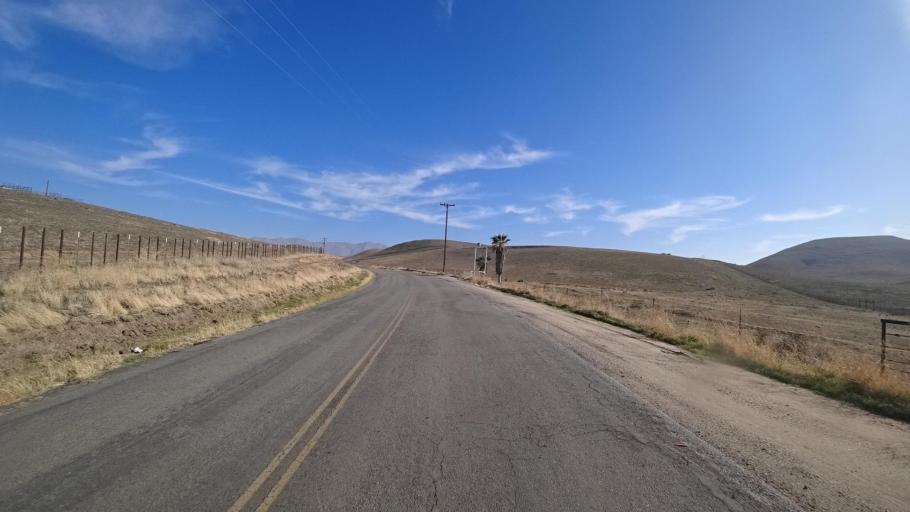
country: US
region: California
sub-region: Kern County
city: Lamont
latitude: 35.3810
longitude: -118.8285
